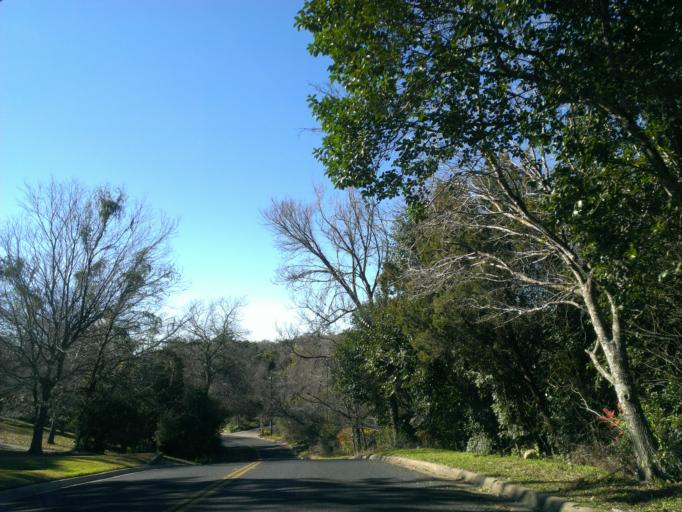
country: US
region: Texas
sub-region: Travis County
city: West Lake Hills
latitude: 30.3290
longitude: -97.7659
